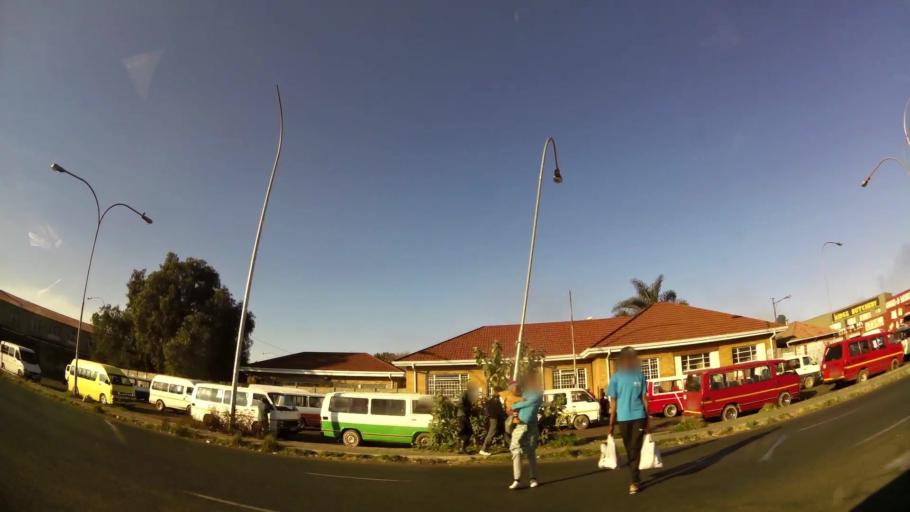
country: ZA
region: Gauteng
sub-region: City of Johannesburg Metropolitan Municipality
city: Roodepoort
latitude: -26.1585
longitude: 27.8688
